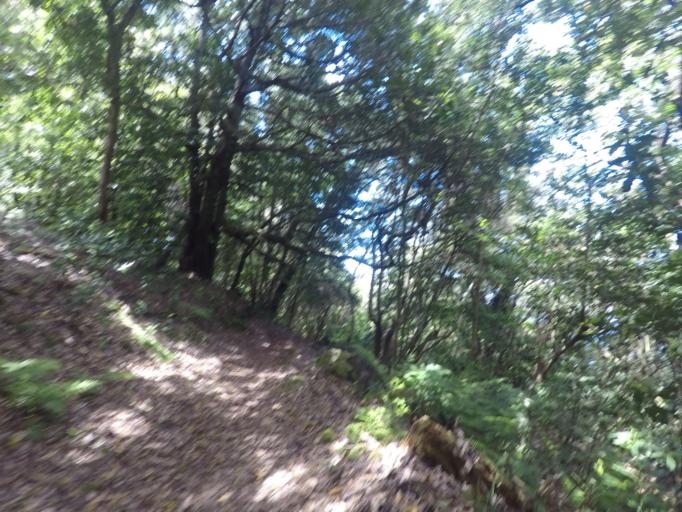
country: PT
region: Madeira
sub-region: Porto Moniz
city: Porto Moniz
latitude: 32.8375
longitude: -17.1441
